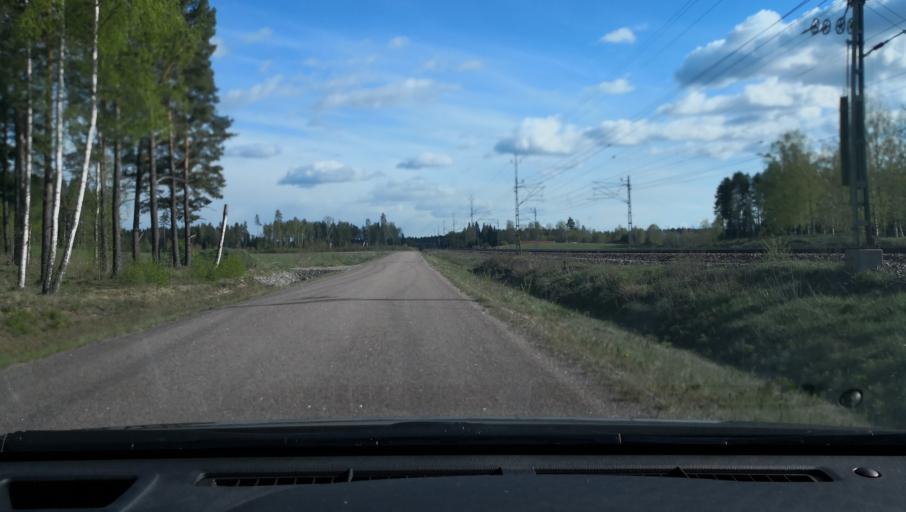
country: SE
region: OErebro
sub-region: Askersunds Kommun
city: Asbro
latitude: 58.9350
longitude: 15.0433
